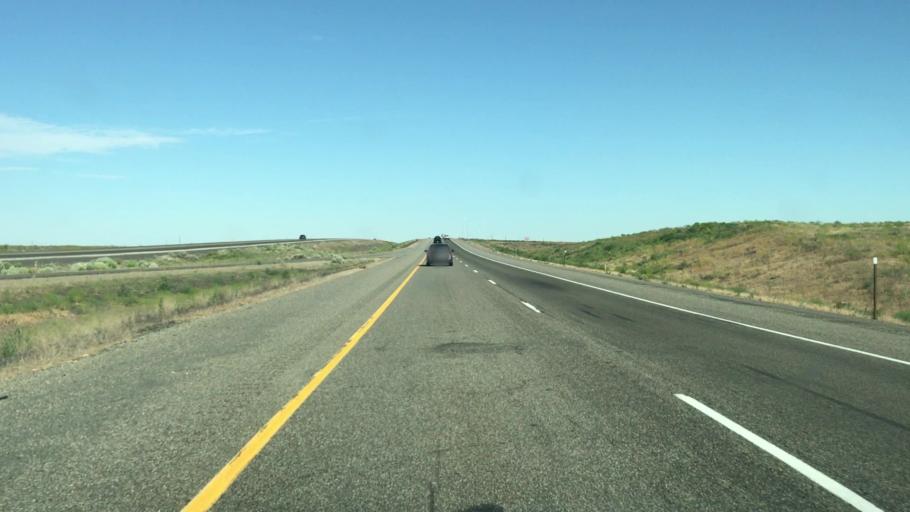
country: US
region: Idaho
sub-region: Twin Falls County
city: Twin Falls
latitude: 42.6392
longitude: -114.4367
